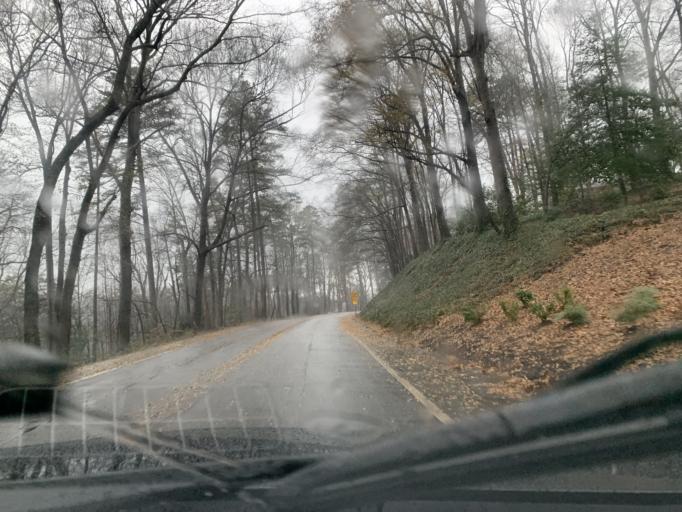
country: US
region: South Carolina
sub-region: Greenville County
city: Greenville
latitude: 34.8436
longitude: -82.3858
